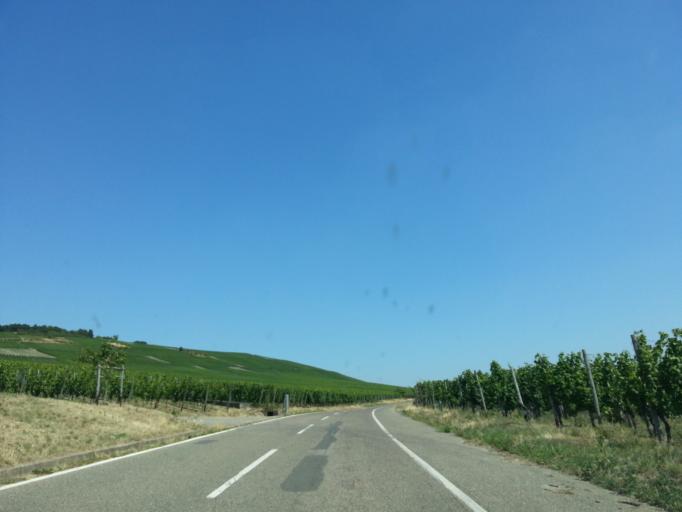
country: DE
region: Rheinland-Pfalz
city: Minheim
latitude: 49.8696
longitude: 6.9381
